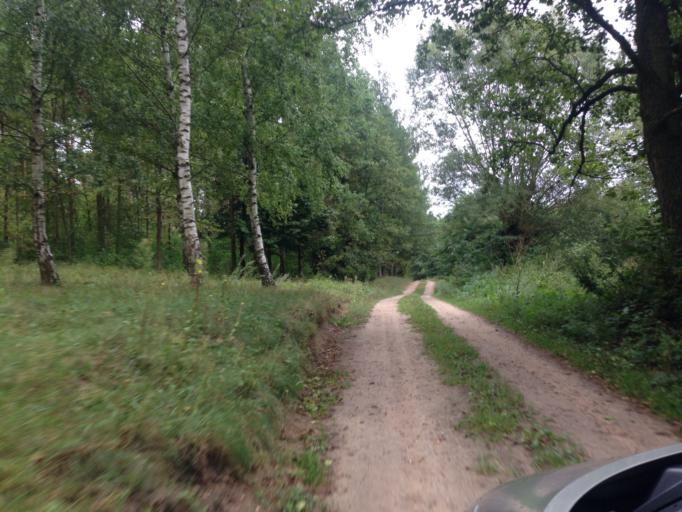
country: PL
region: Kujawsko-Pomorskie
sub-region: Powiat brodnicki
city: Bartniczka
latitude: 53.2775
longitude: 19.6185
